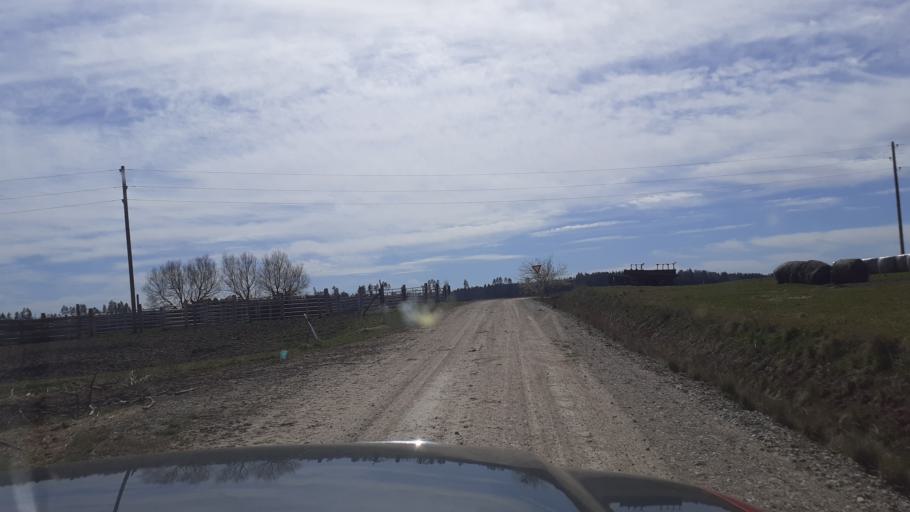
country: LV
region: Kuldigas Rajons
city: Kuldiga
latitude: 56.8365
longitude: 22.0022
